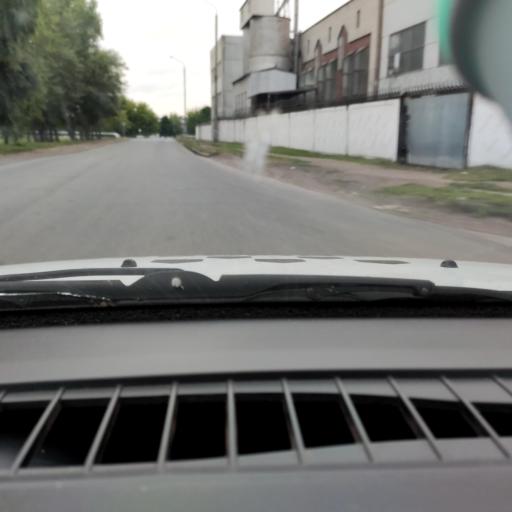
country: RU
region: Tatarstan
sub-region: Tukayevskiy Rayon
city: Naberezhnyye Chelny
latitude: 55.6664
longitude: 52.2729
